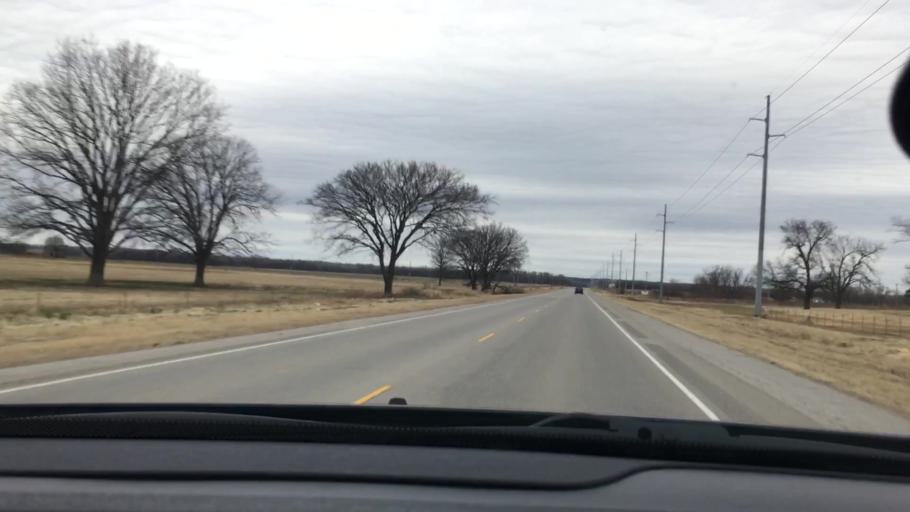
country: US
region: Oklahoma
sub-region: Marshall County
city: Oakland
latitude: 34.1983
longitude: -96.8022
